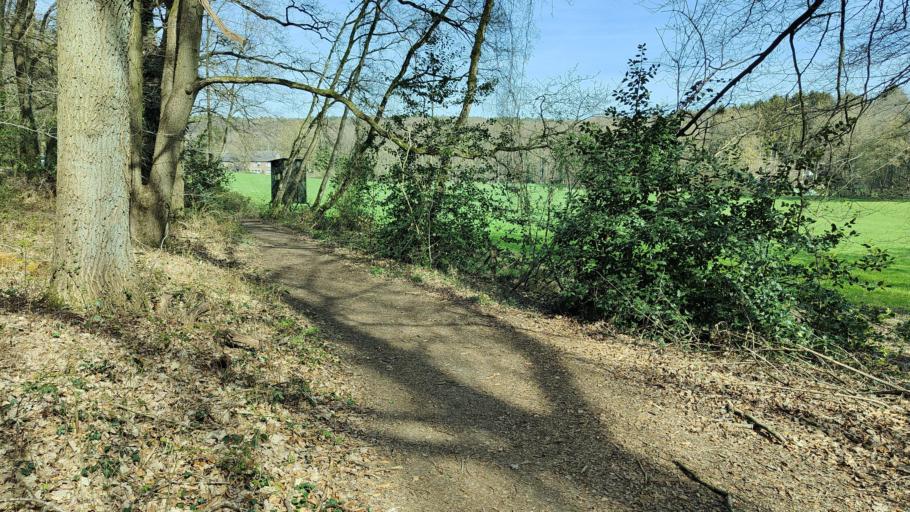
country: DE
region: North Rhine-Westphalia
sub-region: Regierungsbezirk Koln
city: Wassenberg
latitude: 51.1130
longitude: 6.1628
